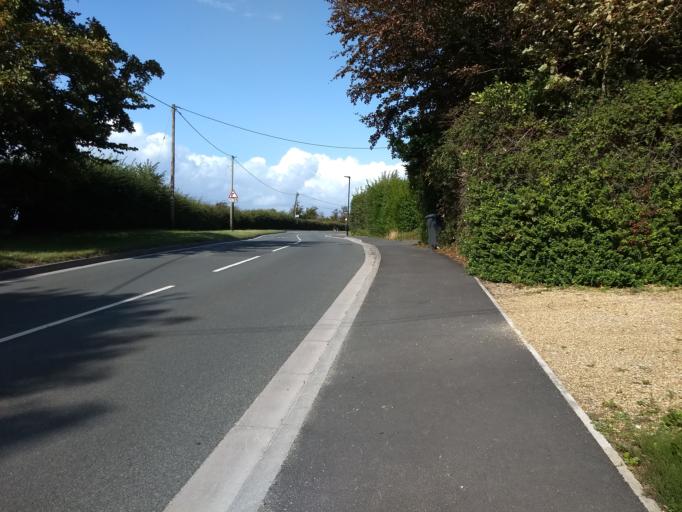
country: GB
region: England
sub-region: Isle of Wight
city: Totland
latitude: 50.6895
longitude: -1.5309
